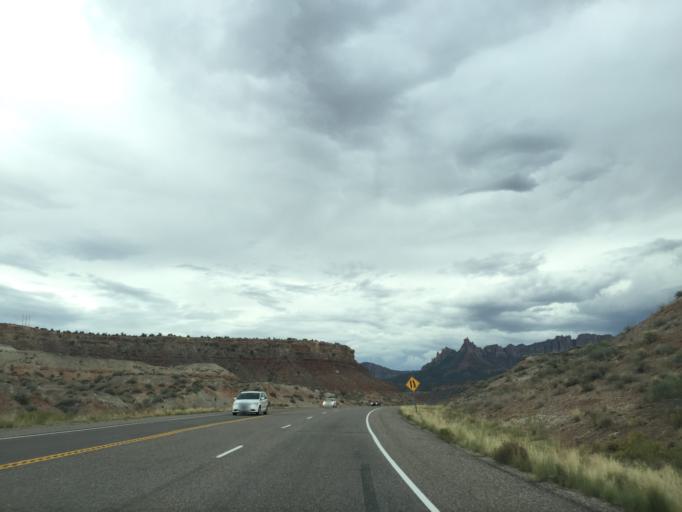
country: US
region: Utah
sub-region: Washington County
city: Hildale
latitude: 37.1702
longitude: -113.0679
